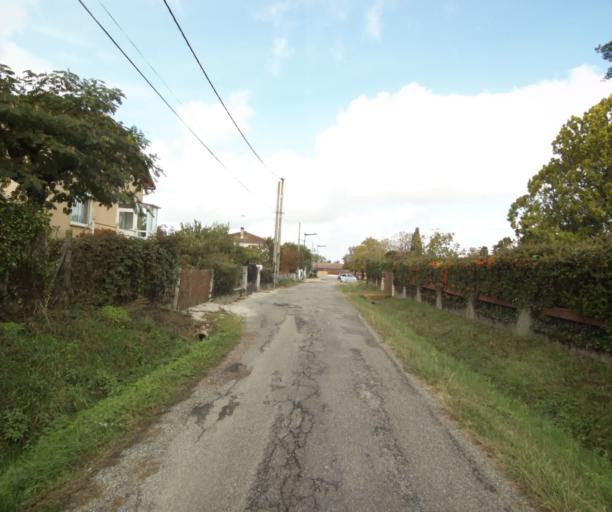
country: FR
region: Midi-Pyrenees
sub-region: Departement du Tarn-et-Garonne
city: Finhan
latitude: 43.8985
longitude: 1.1330
